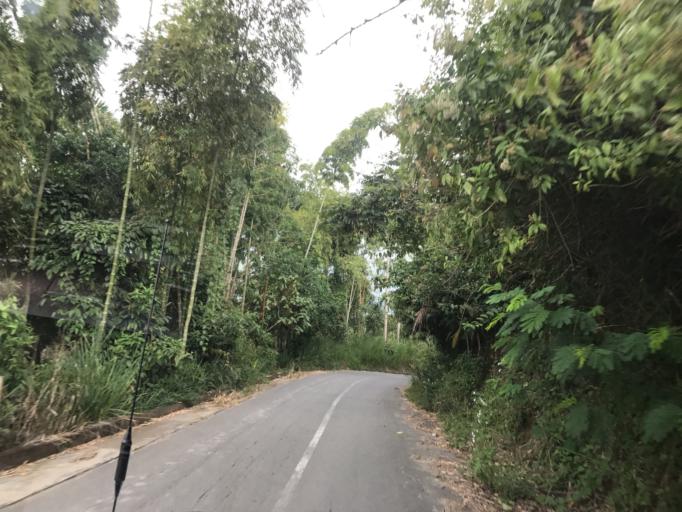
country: CO
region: Quindio
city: Montenegro
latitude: 4.5454
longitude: -75.8636
